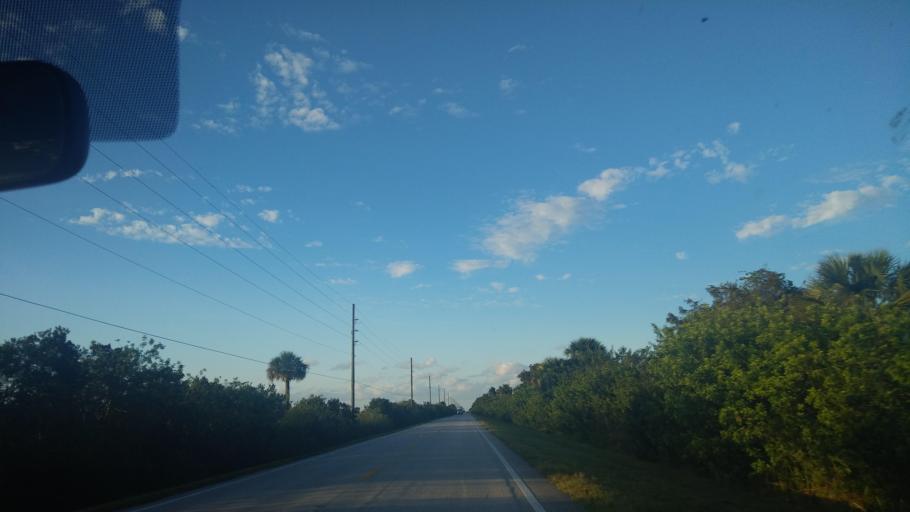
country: US
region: Florida
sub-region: Indian River County
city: Fellsmere
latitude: 27.6736
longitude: -80.6431
